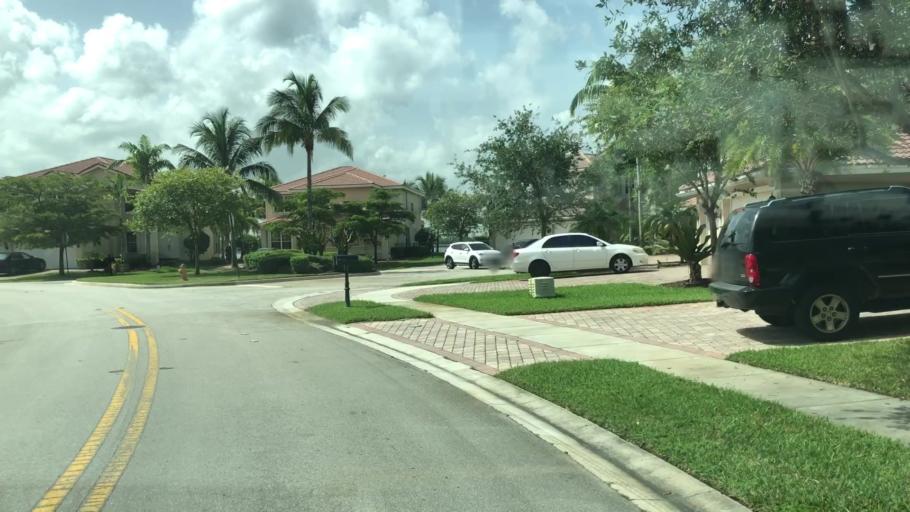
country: US
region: Florida
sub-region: Miami-Dade County
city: Palm Springs North
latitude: 25.9660
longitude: -80.3838
